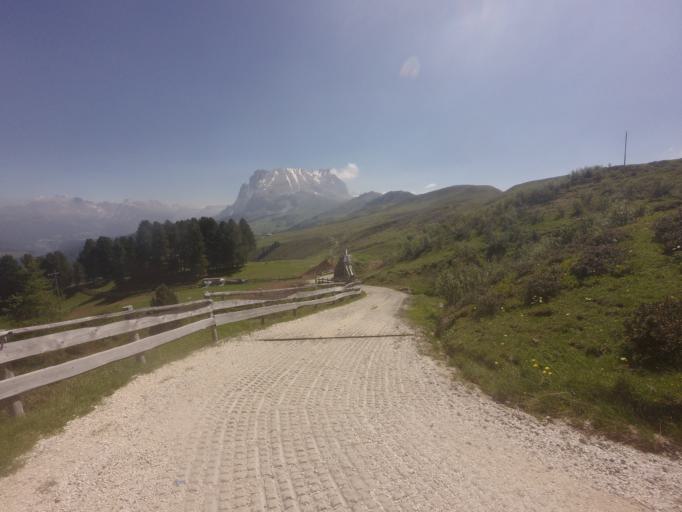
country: IT
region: Trentino-Alto Adige
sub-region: Provincia di Trento
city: Mazzin
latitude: 46.5000
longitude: 11.6497
